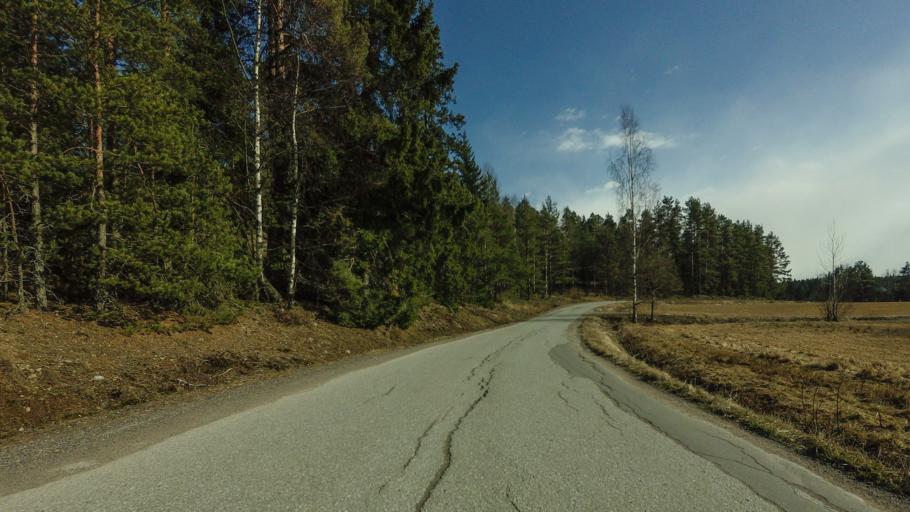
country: FI
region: Uusimaa
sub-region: Helsinki
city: Karjalohja
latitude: 60.2674
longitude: 23.6680
